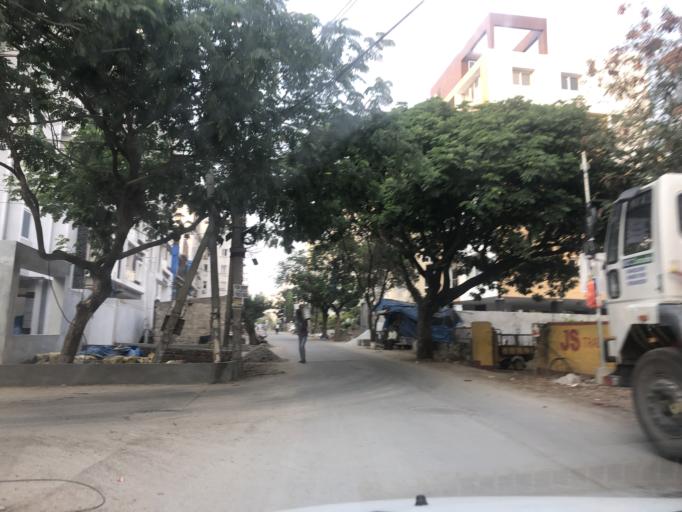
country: IN
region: Telangana
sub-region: Rangareddi
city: Kukatpalli
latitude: 17.4466
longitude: 78.3995
